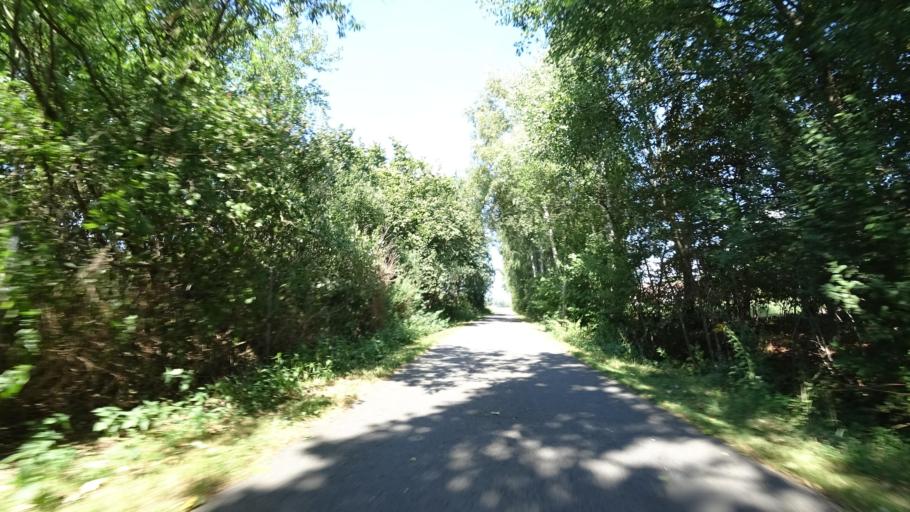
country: DE
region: North Rhine-Westphalia
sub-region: Regierungsbezirk Detmold
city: Rheda-Wiedenbruck
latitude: 51.8871
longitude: 8.2908
